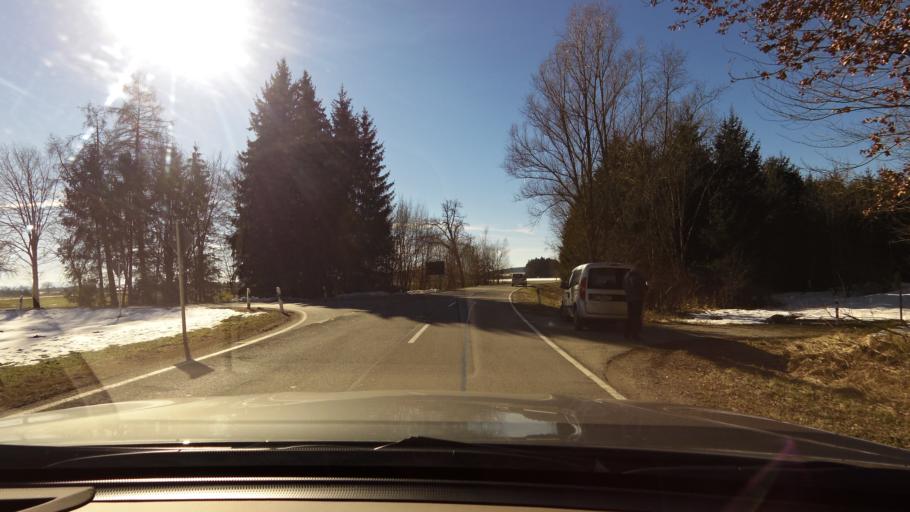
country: DE
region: Bavaria
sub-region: Upper Bavaria
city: Taufkirchen
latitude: 48.1567
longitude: 12.4564
